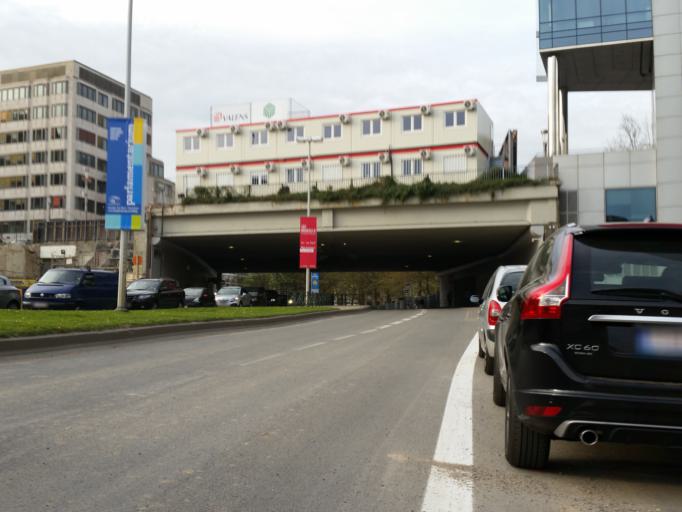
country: BE
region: Brussels Capital
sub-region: Bruxelles-Capitale
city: Brussels
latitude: 50.8428
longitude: 4.3783
